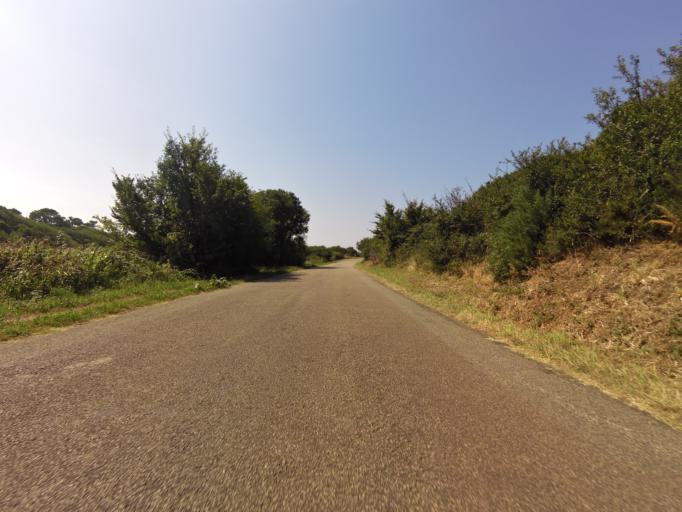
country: FR
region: Brittany
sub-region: Departement du Finistere
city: Pouldreuzic
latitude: 47.9136
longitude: -4.3500
